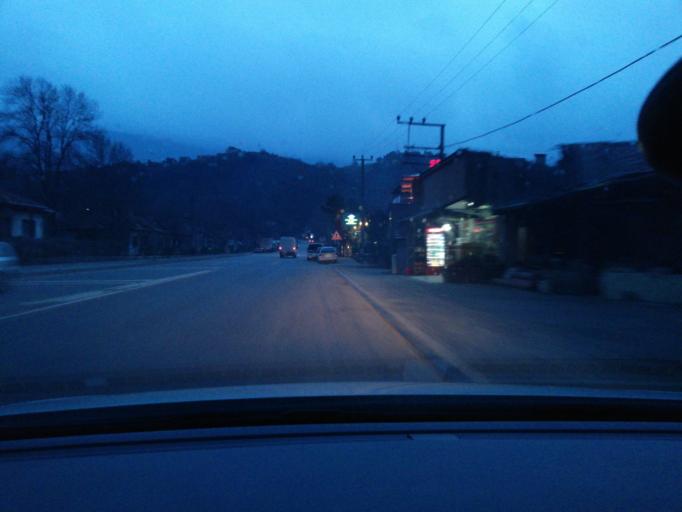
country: TR
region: Bolu
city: Bolu
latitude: 40.6889
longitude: 31.6200
